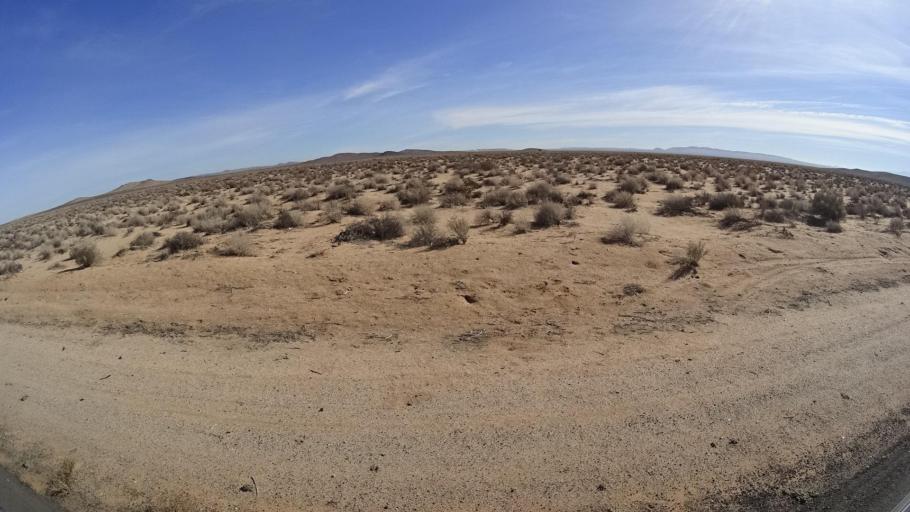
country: US
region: California
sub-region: Kern County
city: North Edwards
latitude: 35.0668
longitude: -117.8042
